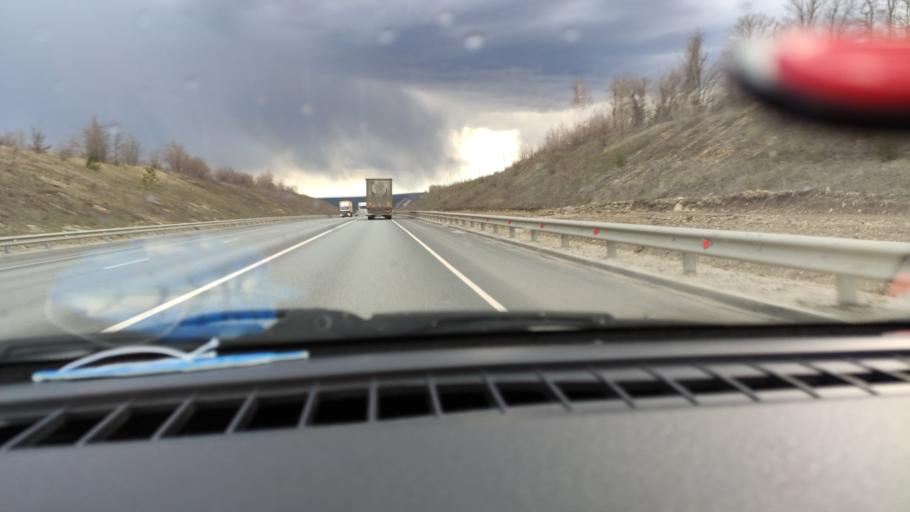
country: RU
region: Saratov
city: Yelshanka
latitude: 51.8870
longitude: 46.5177
